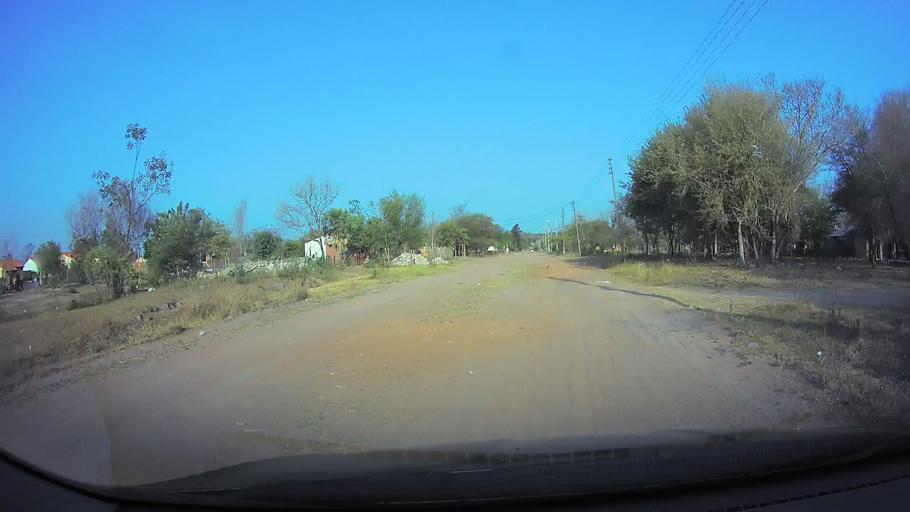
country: PY
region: Central
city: Limpio
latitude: -25.2181
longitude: -57.4913
